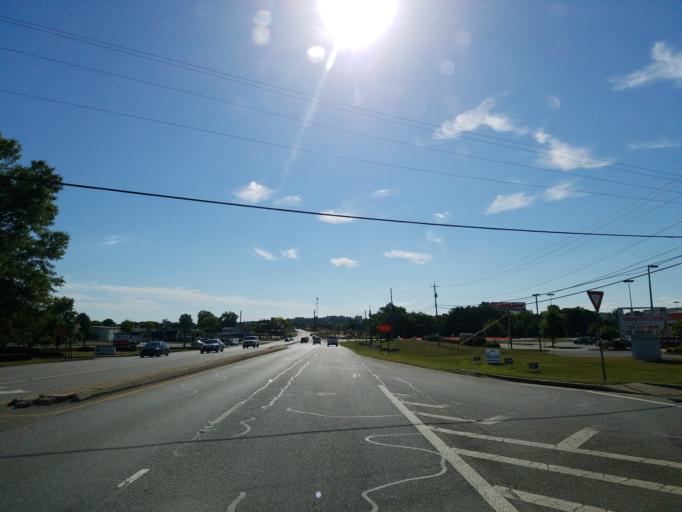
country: US
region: Georgia
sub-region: Bartow County
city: Adairsville
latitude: 34.3770
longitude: -84.9304
